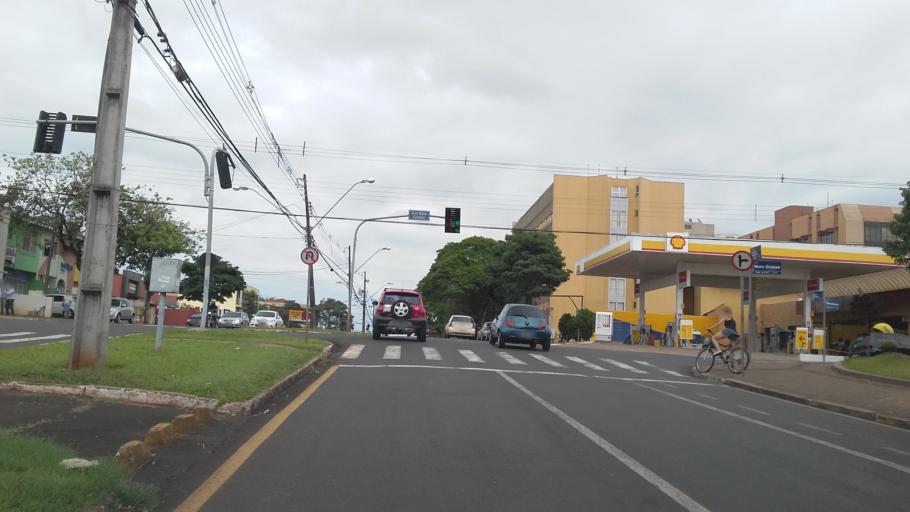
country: BR
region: Parana
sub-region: Londrina
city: Londrina
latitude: -23.3199
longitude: -51.1560
